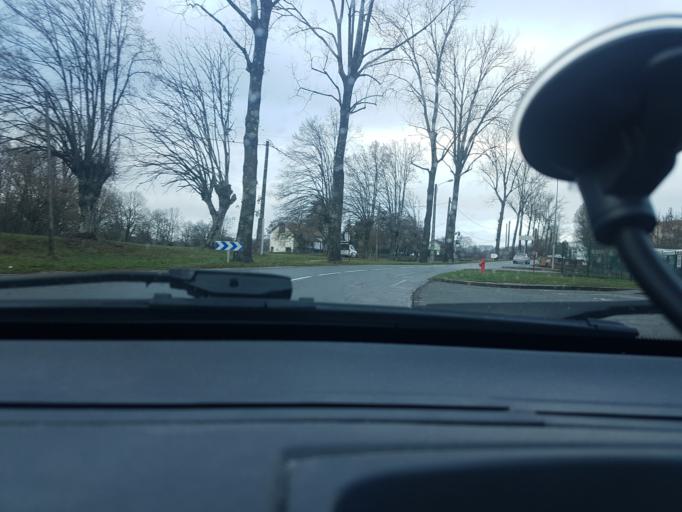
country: FR
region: Franche-Comte
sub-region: Territoire de Belfort
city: Bavilliers
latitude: 47.6127
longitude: 6.8396
